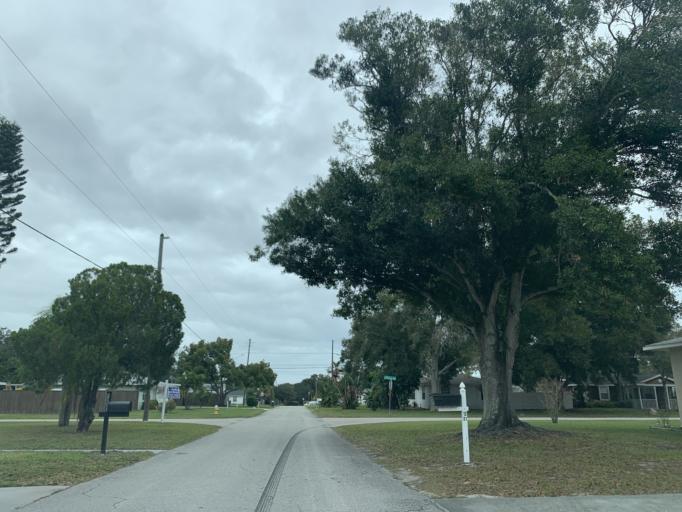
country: US
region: Florida
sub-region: Pinellas County
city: Belleair
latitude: 27.9426
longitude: -82.7868
